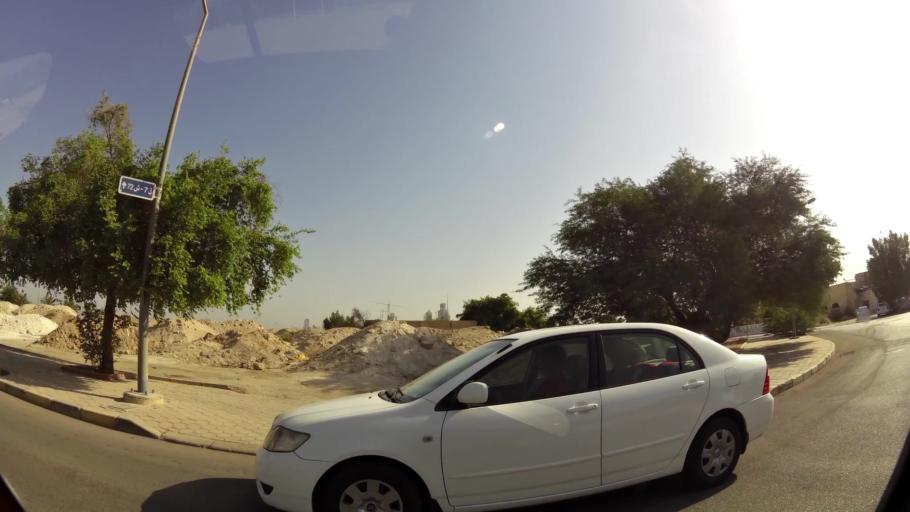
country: KW
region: Al Asimah
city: Ash Shamiyah
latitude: 29.3563
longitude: 47.9466
